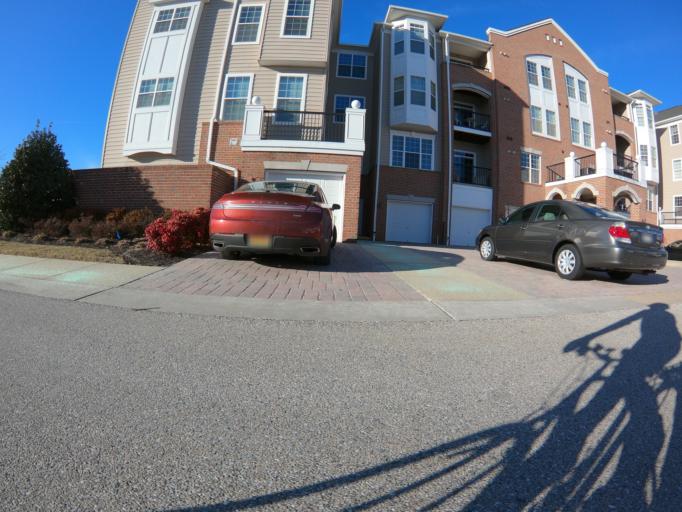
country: US
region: Maryland
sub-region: Howard County
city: West Elkridge
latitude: 39.2040
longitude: -76.7622
